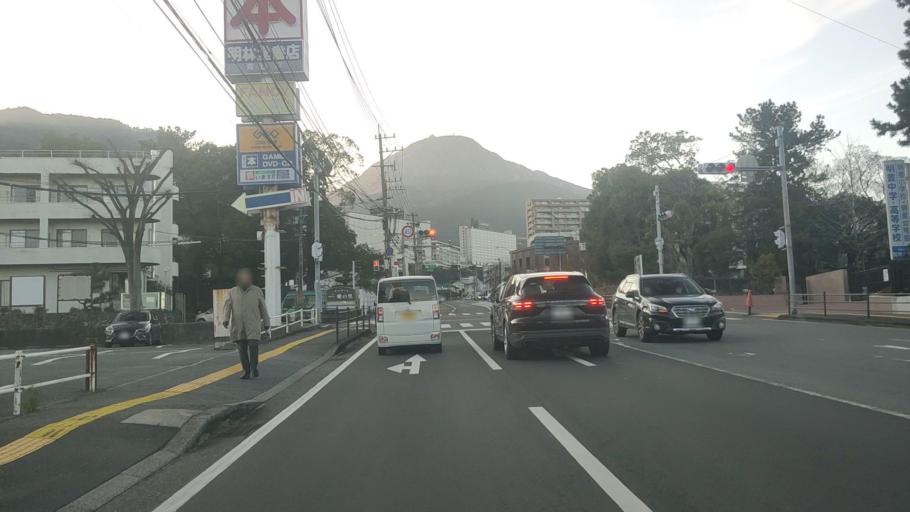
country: JP
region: Oita
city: Beppu
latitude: 33.2833
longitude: 131.4845
